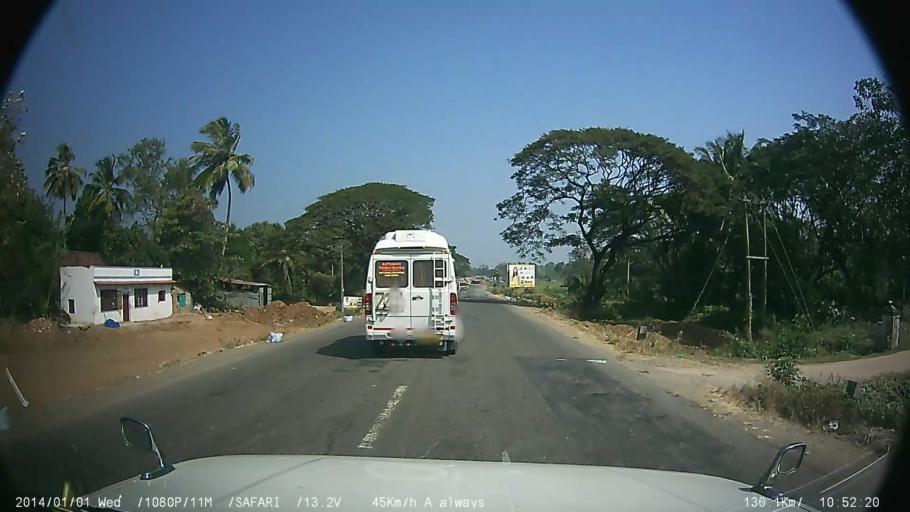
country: IN
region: Kerala
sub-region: Palakkad district
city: Palakkad
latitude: 10.7091
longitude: 76.5950
